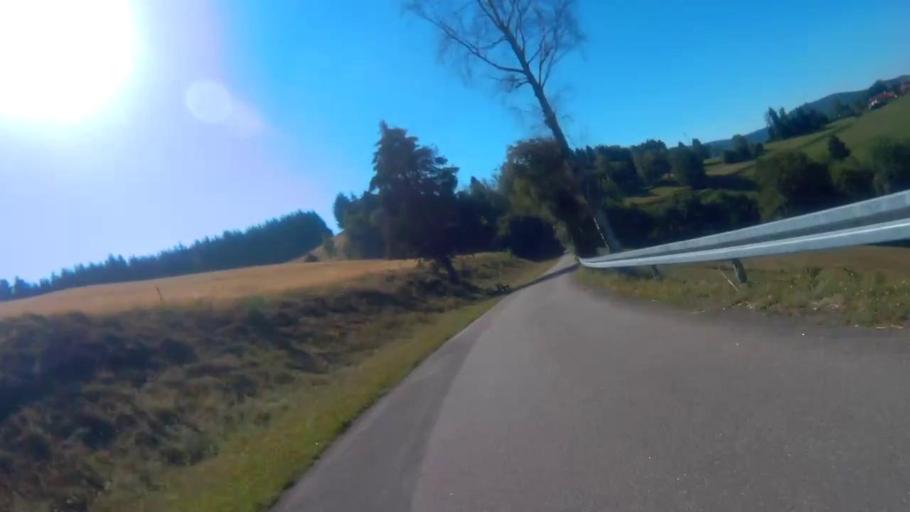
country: DE
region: Baden-Wuerttemberg
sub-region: Freiburg Region
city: Wembach
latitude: 47.7492
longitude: 7.9059
